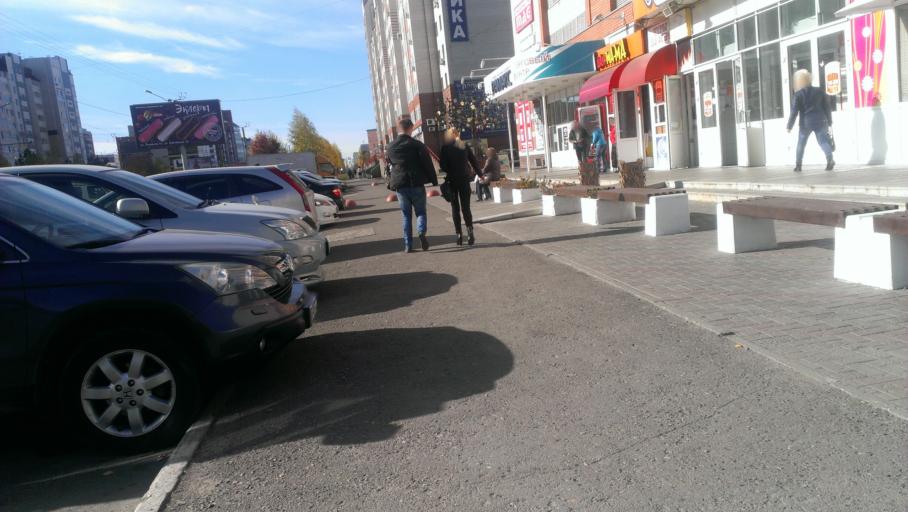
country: RU
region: Altai Krai
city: Novosilikatnyy
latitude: 53.3342
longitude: 83.6896
